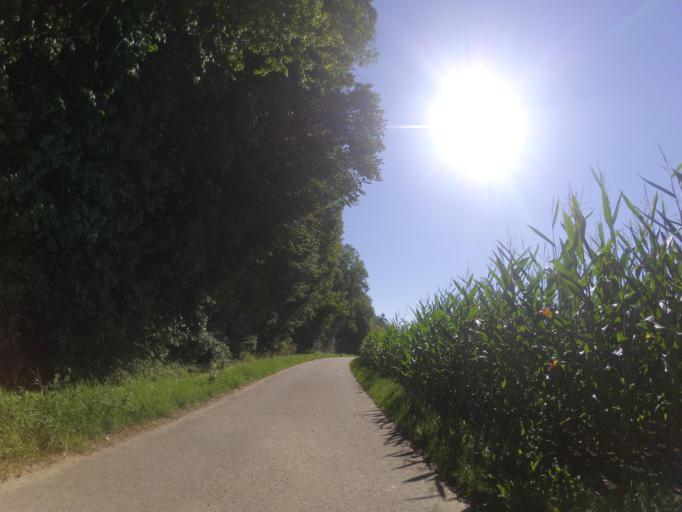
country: DE
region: Baden-Wuerttemberg
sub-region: Tuebingen Region
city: Bernstadt
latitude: 48.4513
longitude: 10.0640
